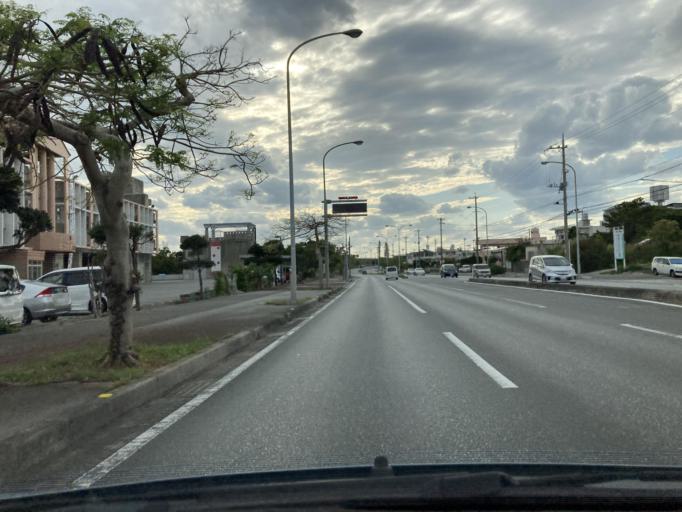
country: JP
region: Okinawa
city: Okinawa
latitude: 26.3644
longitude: 127.7678
